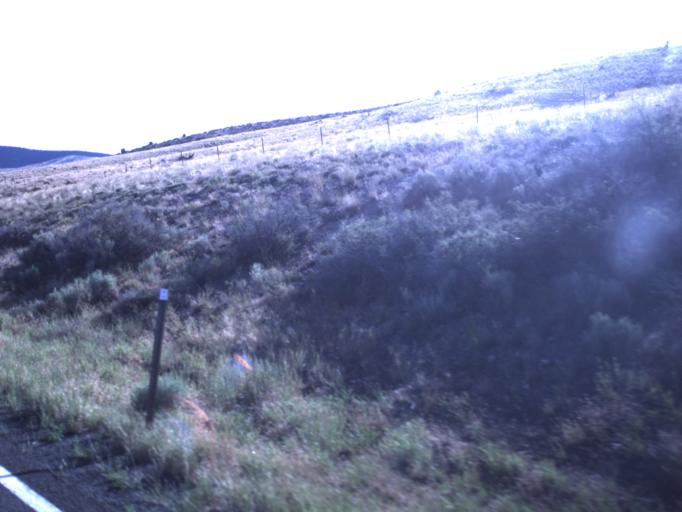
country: US
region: Utah
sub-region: Iron County
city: Parowan
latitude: 38.0836
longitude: -112.9566
